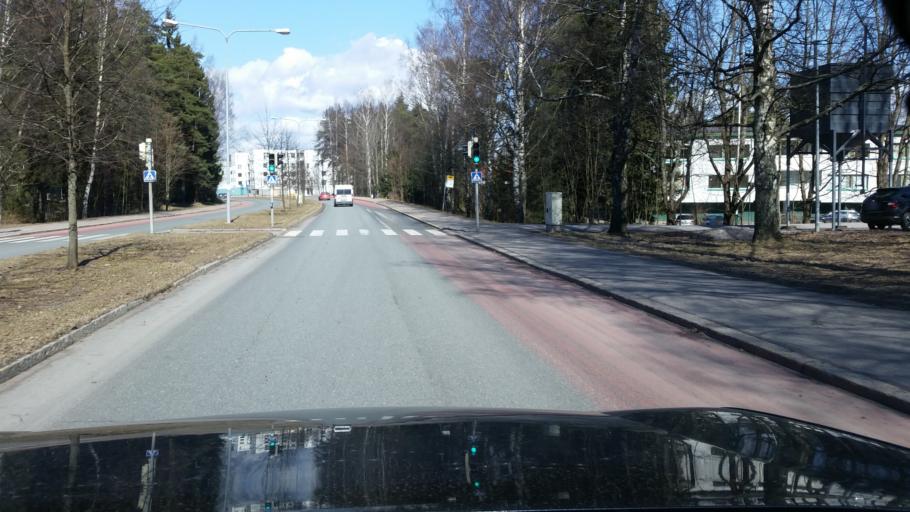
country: FI
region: Uusimaa
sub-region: Helsinki
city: Teekkarikylae
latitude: 60.2350
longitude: 24.8468
